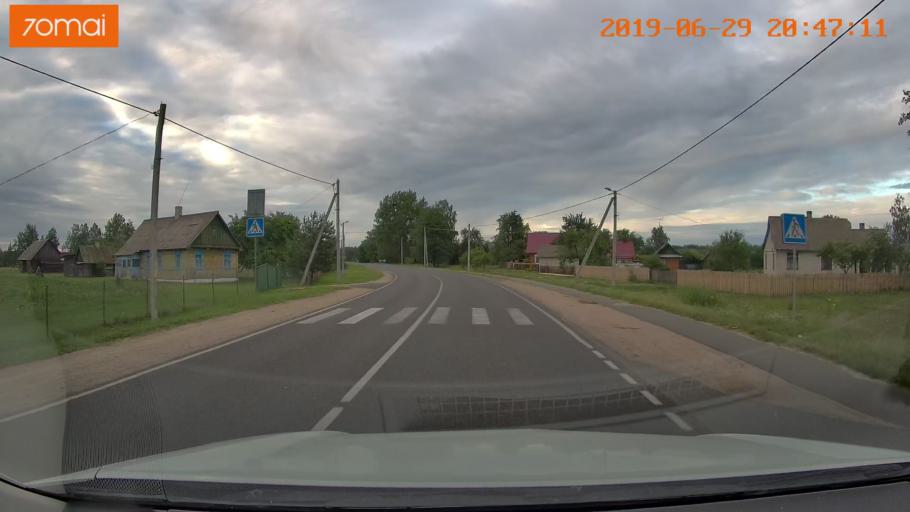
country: BY
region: Brest
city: Hantsavichy
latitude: 52.6361
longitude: 26.3149
